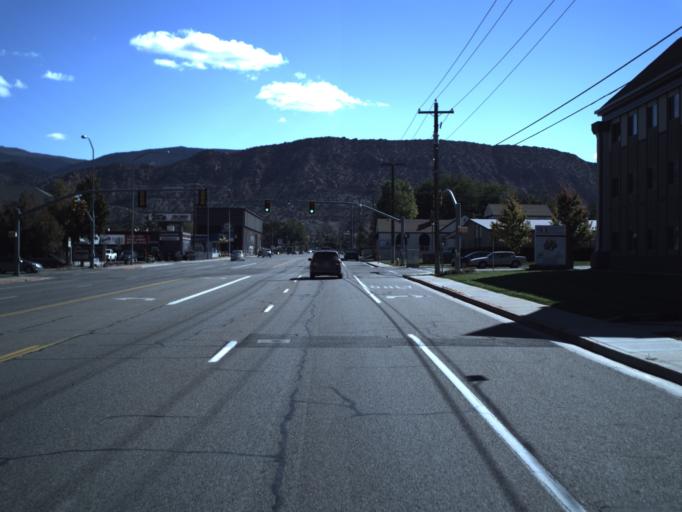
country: US
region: Utah
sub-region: Iron County
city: Cedar City
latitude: 37.6808
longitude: -113.0678
